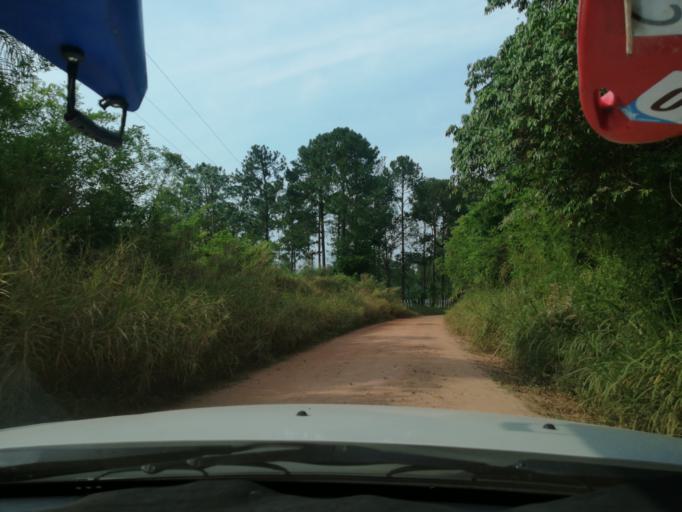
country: AR
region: Misiones
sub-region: Departamento de San Ignacio
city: San Ignacio
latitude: -27.2912
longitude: -55.5629
